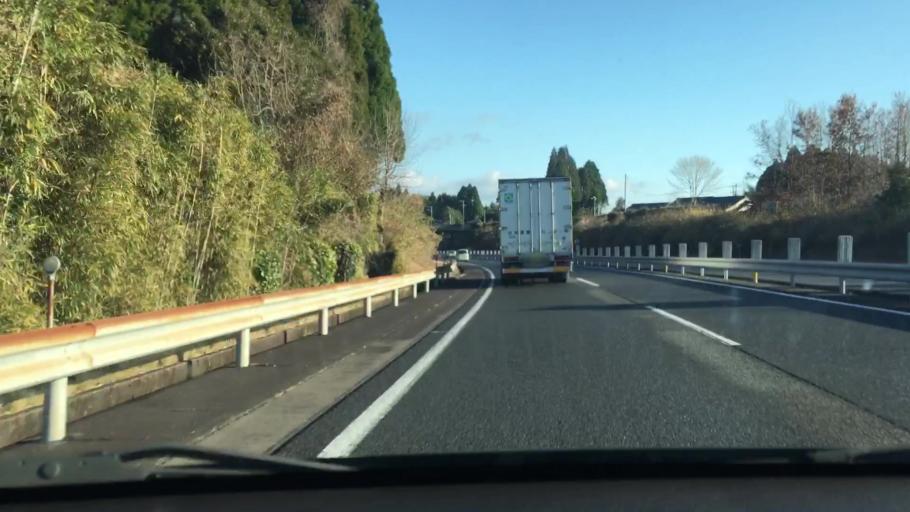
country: JP
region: Kagoshima
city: Kajiki
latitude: 31.8211
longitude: 130.6957
